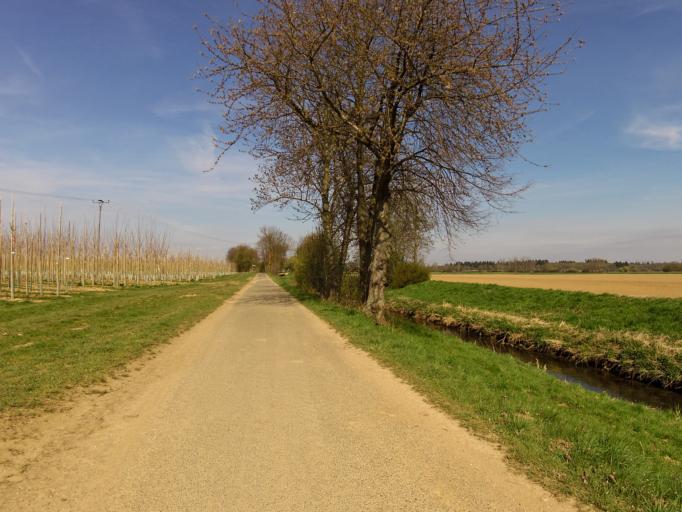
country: DE
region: North Rhine-Westphalia
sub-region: Regierungsbezirk Koln
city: Rheinbach
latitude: 50.6546
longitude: 6.9756
